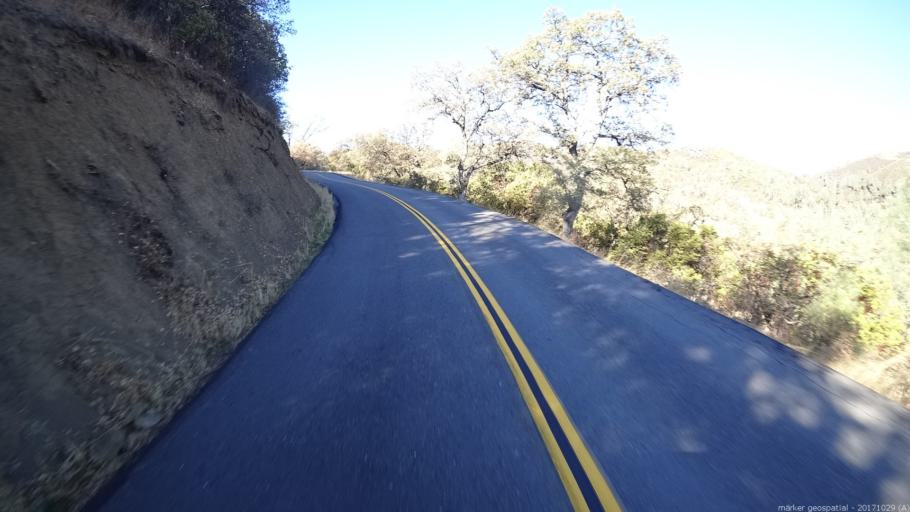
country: US
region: California
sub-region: Trinity County
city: Lewiston
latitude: 40.3893
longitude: -122.8184
